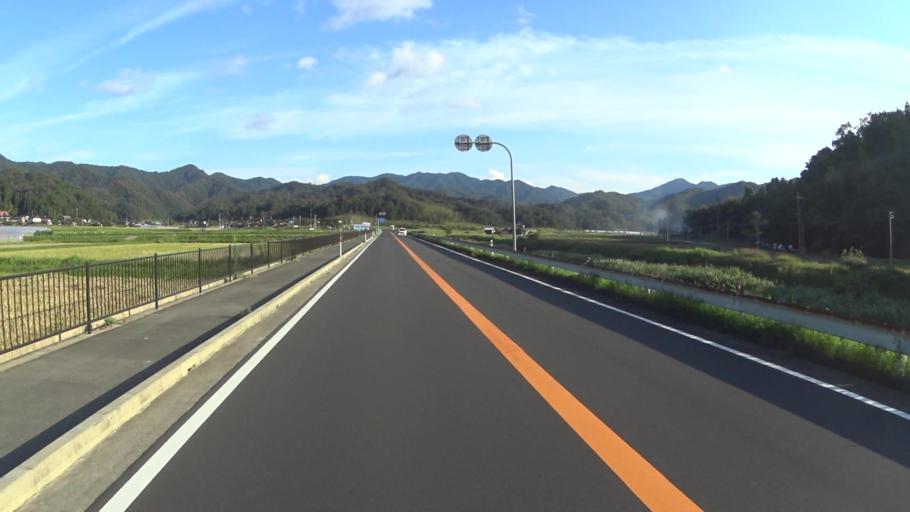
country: JP
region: Hyogo
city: Toyooka
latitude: 35.5777
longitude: 134.9737
